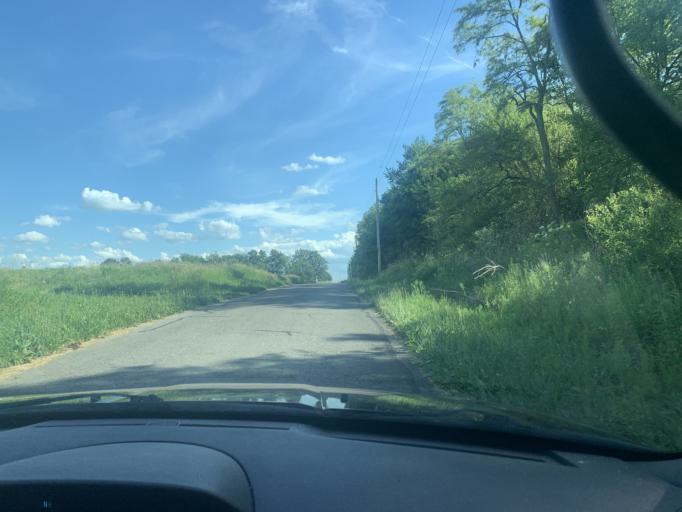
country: US
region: Ohio
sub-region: Logan County
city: De Graff
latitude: 40.3415
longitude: -83.8715
